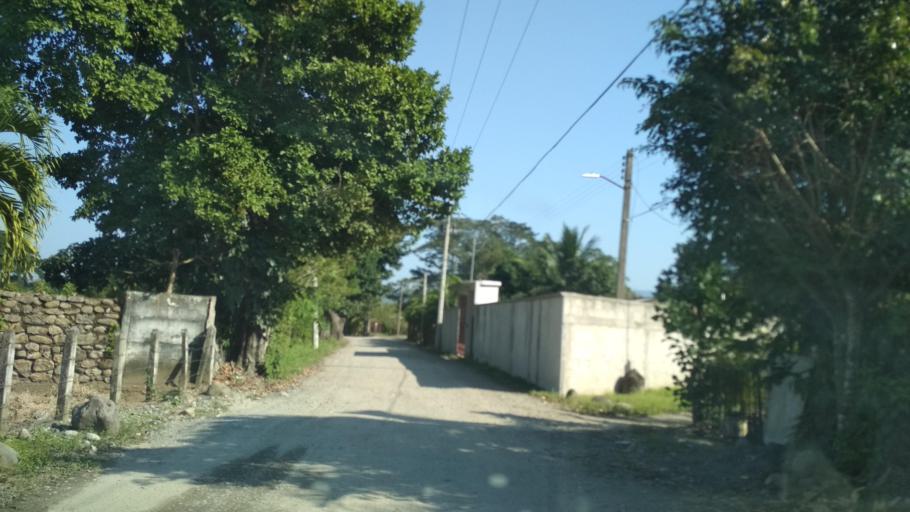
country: MX
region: Veracruz
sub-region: Martinez de la Torre
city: El Progreso
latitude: 20.0809
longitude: -97.0197
